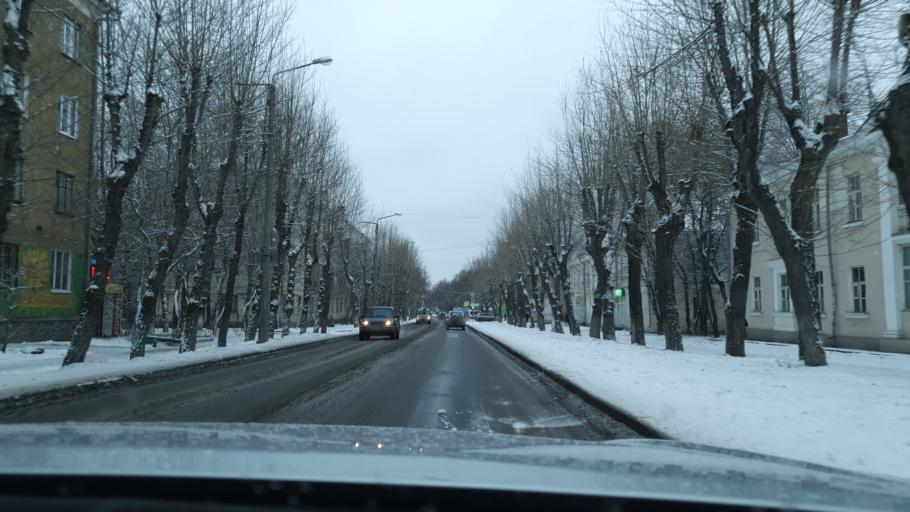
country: RU
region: Sverdlovsk
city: Istok
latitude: 56.7544
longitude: 60.7084
